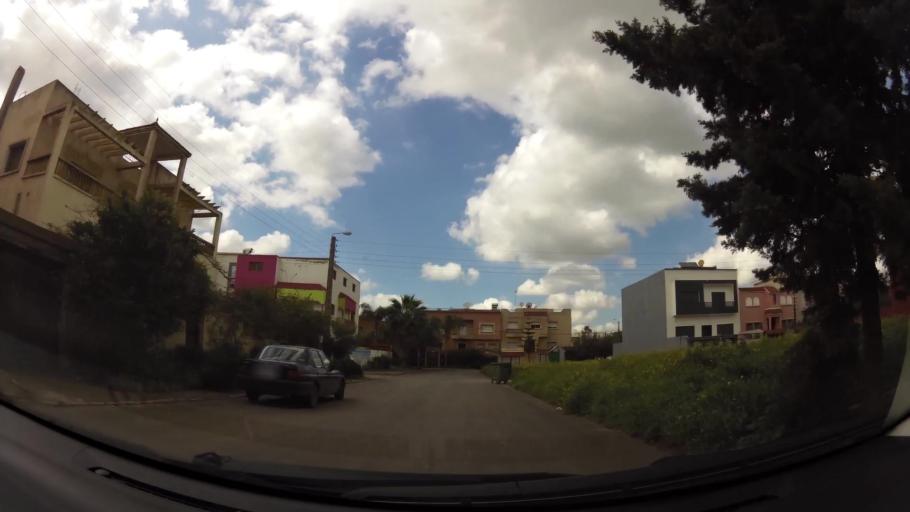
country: MA
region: Chaouia-Ouardigha
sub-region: Settat Province
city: Berrechid
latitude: 33.2763
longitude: -7.5909
